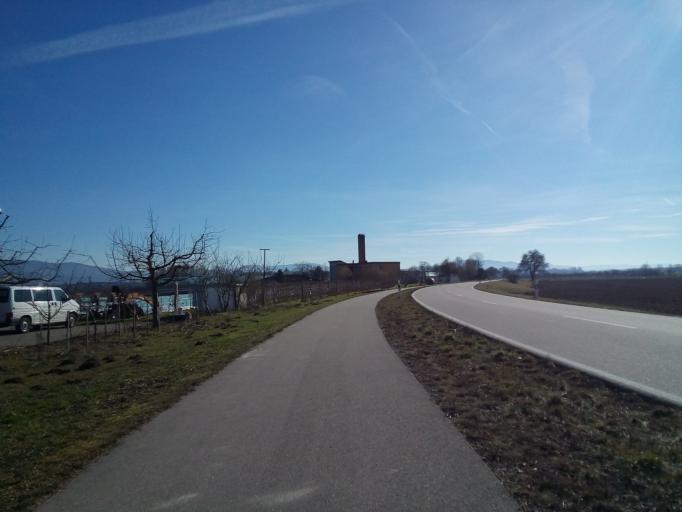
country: DE
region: Baden-Wuerttemberg
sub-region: Freiburg Region
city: Renchen
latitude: 48.6173
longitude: 8.0191
